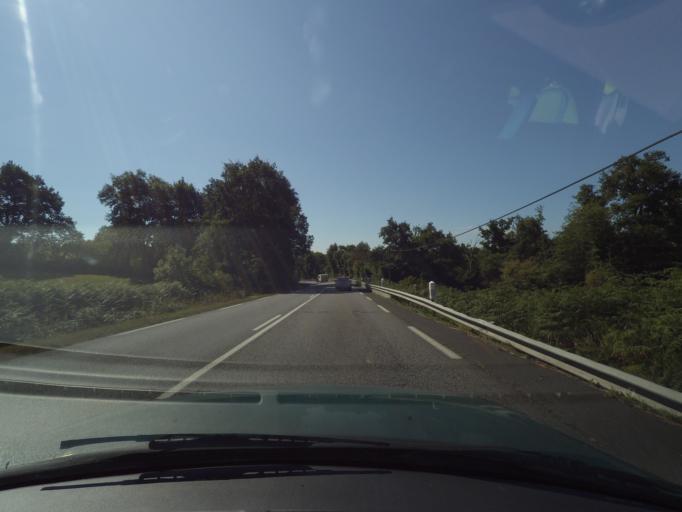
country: FR
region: Limousin
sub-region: Departement de la Haute-Vienne
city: Bellac
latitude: 46.1024
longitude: 1.0751
